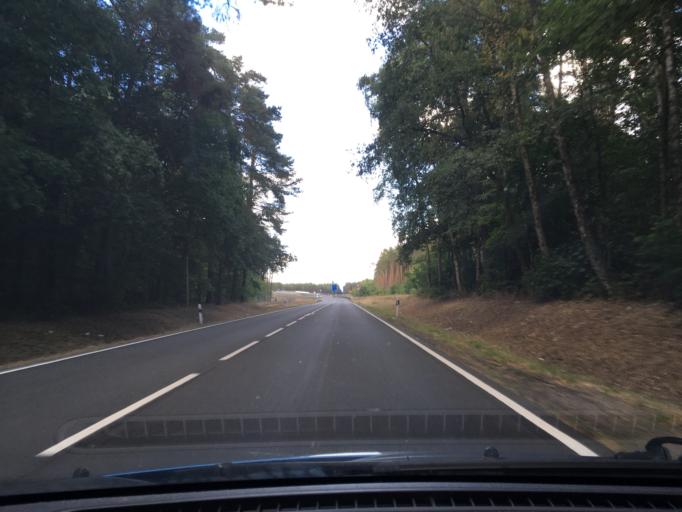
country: DE
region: Mecklenburg-Vorpommern
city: Ludwigslust
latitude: 53.3395
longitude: 11.5137
